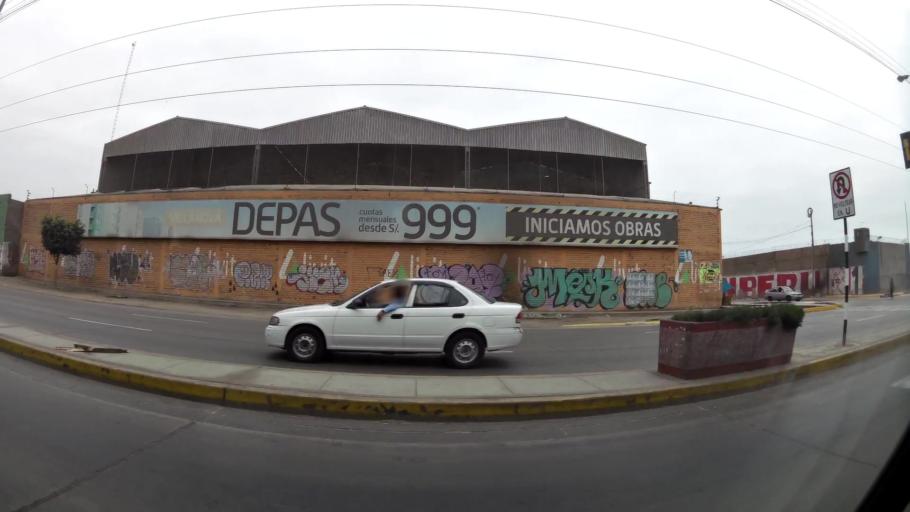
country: PE
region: Callao
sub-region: Callao
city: Callao
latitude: -12.0501
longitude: -77.1179
